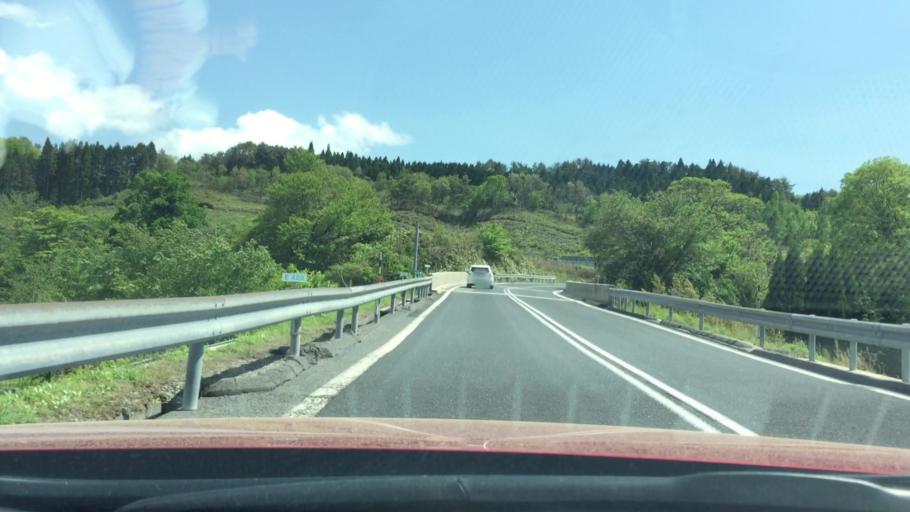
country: JP
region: Tottori
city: Kurayoshi
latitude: 35.2757
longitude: 133.6223
